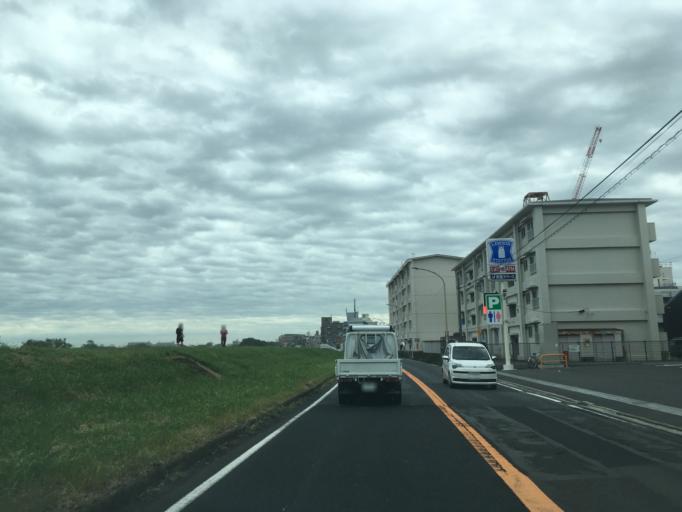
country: JP
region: Tokyo
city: Chofugaoka
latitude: 35.6339
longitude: 139.5489
